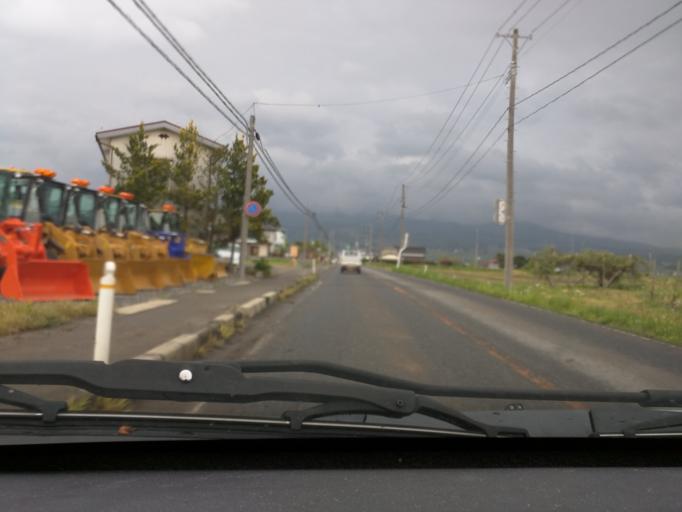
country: JP
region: Fukushima
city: Kitakata
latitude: 37.6473
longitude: 139.8988
